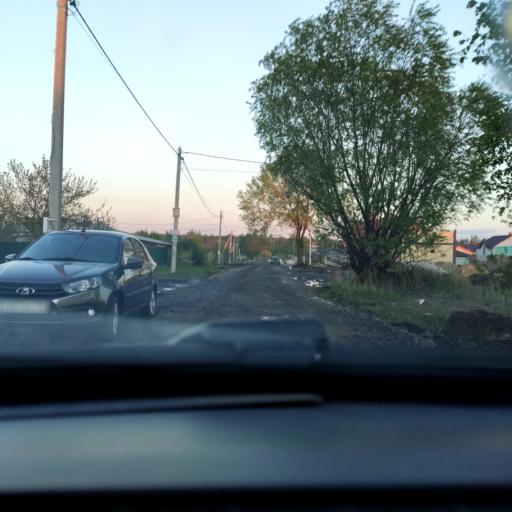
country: RU
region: Voronezj
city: Novaya Usman'
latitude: 51.6564
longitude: 39.4219
